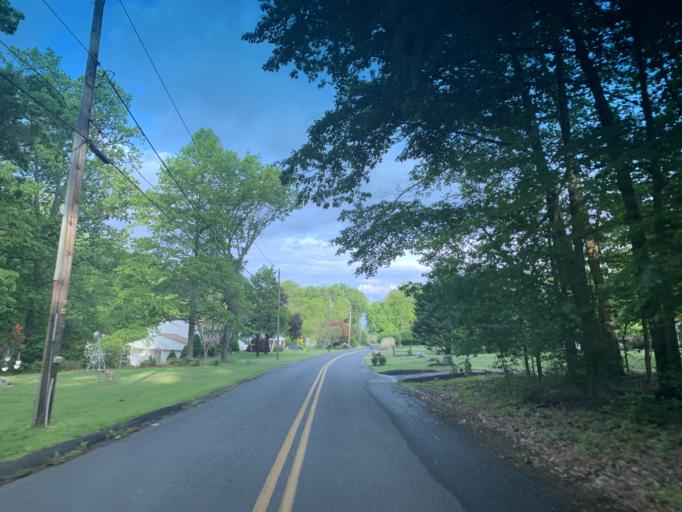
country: US
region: Pennsylvania
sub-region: York County
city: Susquehanna Trails
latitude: 39.6755
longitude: -76.2405
